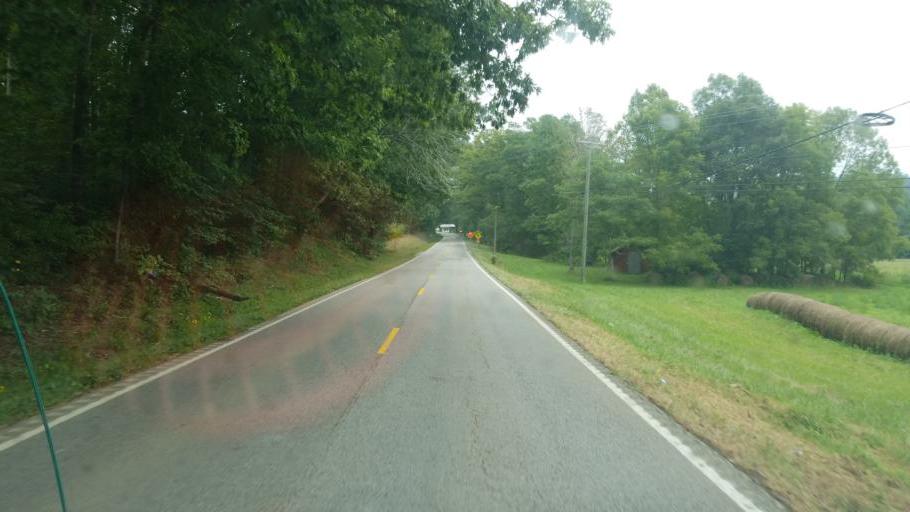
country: US
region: Kentucky
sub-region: Rowan County
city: Morehead
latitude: 38.2441
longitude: -83.4447
